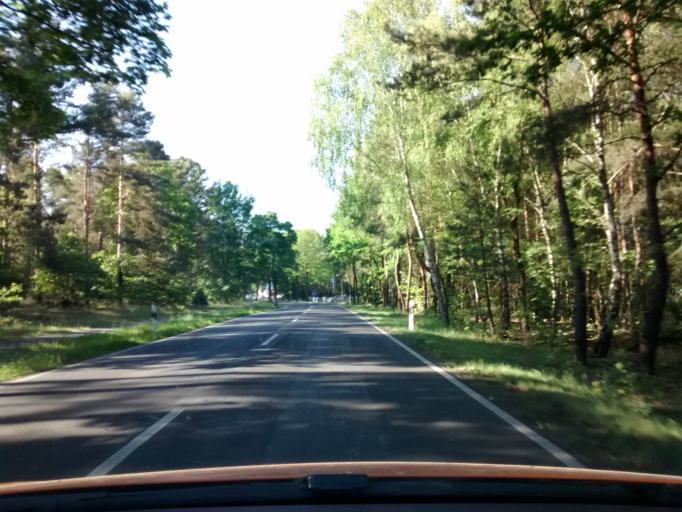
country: DE
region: Brandenburg
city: Langewahl
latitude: 52.3247
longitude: 14.0790
